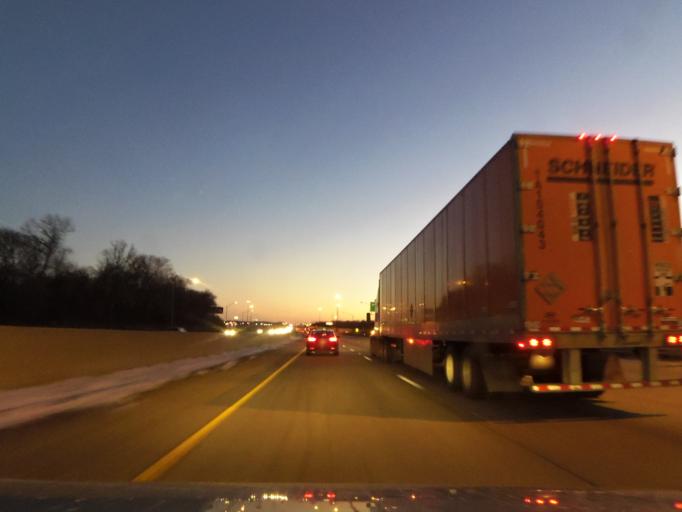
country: US
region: Indiana
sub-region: Lake County
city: Merrillville
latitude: 41.5142
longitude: -87.3198
